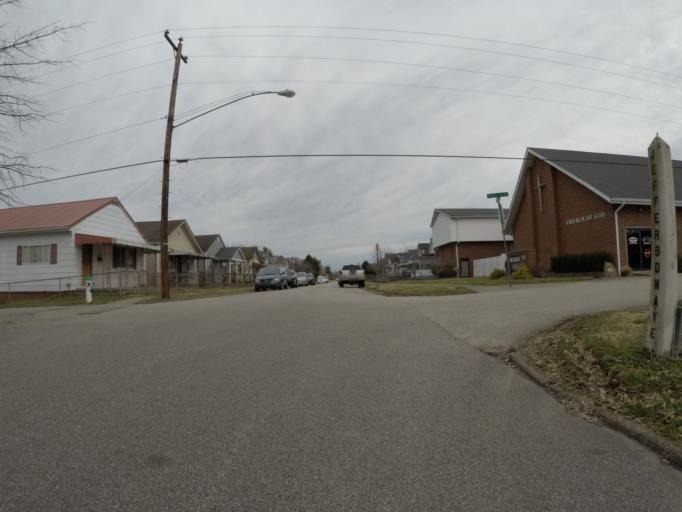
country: US
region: Ohio
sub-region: Lawrence County
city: Burlington
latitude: 38.4074
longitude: -82.4899
